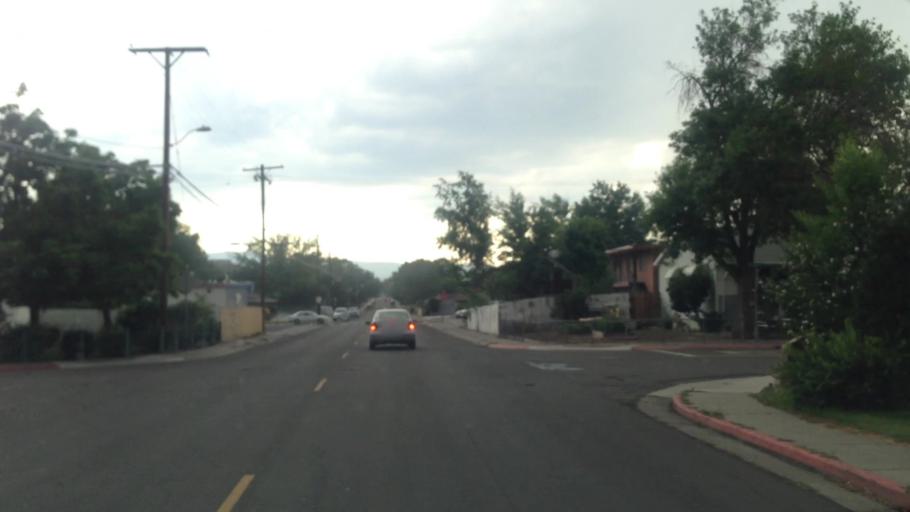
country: US
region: Nevada
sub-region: Washoe County
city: Reno
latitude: 39.5174
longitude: -119.7924
